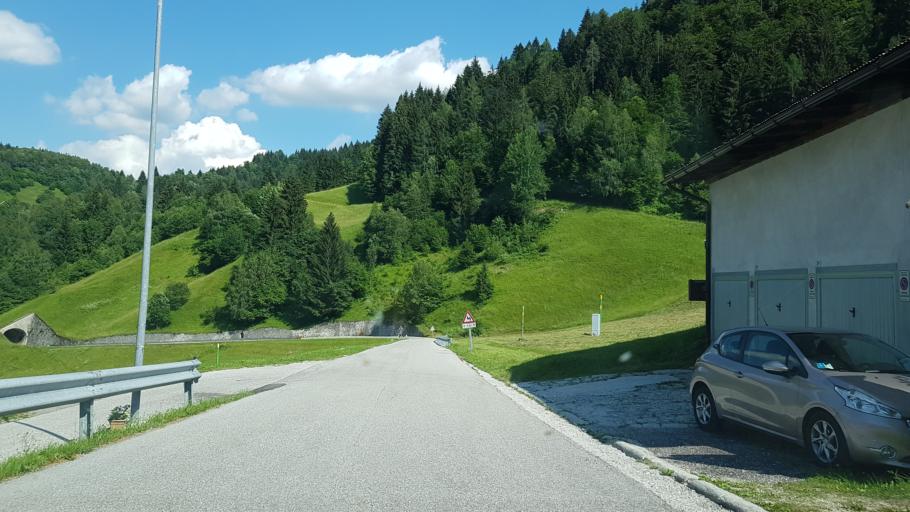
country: IT
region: Friuli Venezia Giulia
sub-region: Provincia di Udine
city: Pontebba
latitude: 46.5078
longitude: 13.2774
